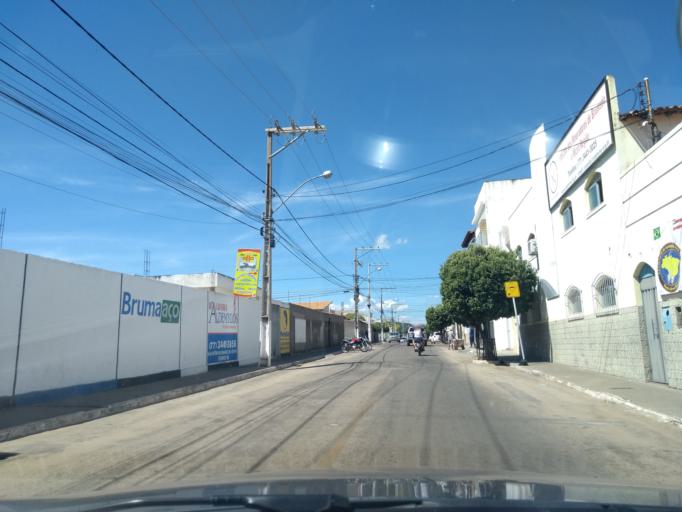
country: BR
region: Bahia
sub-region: Brumado
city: Brumado
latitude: -14.2057
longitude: -41.6691
